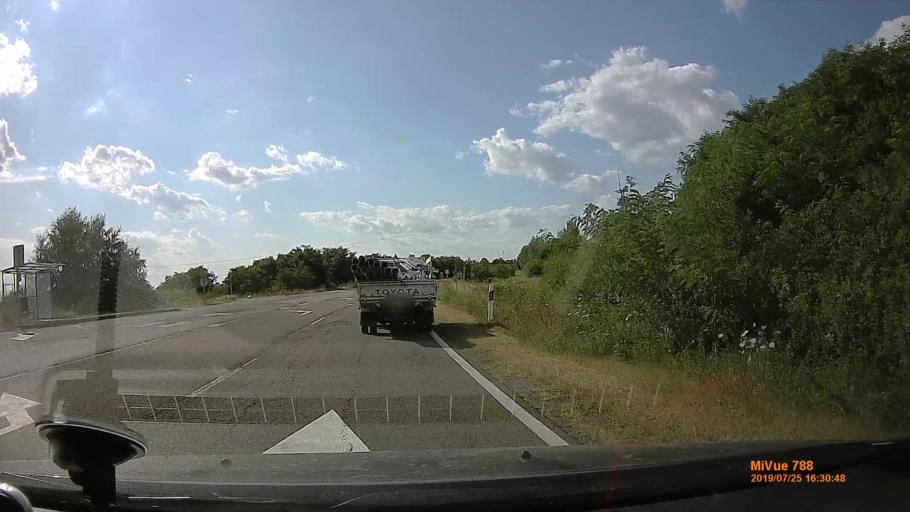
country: HU
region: Heves
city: Karacsond
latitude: 47.7309
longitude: 20.0484
